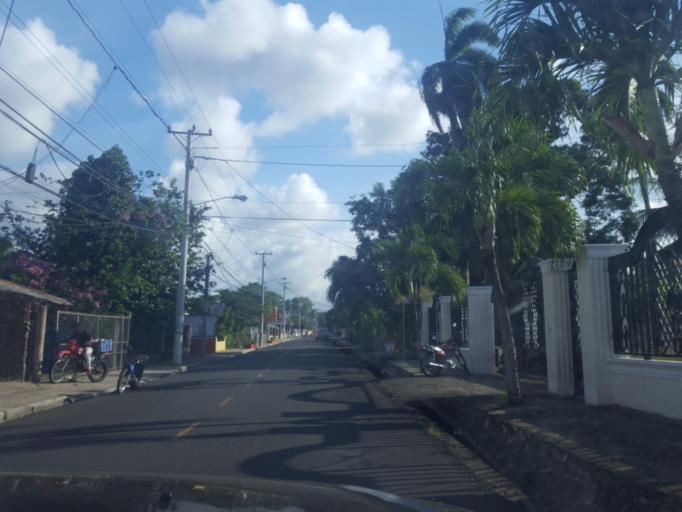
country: DO
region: Santiago
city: Licey al Medio
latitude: 19.3837
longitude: -70.6313
